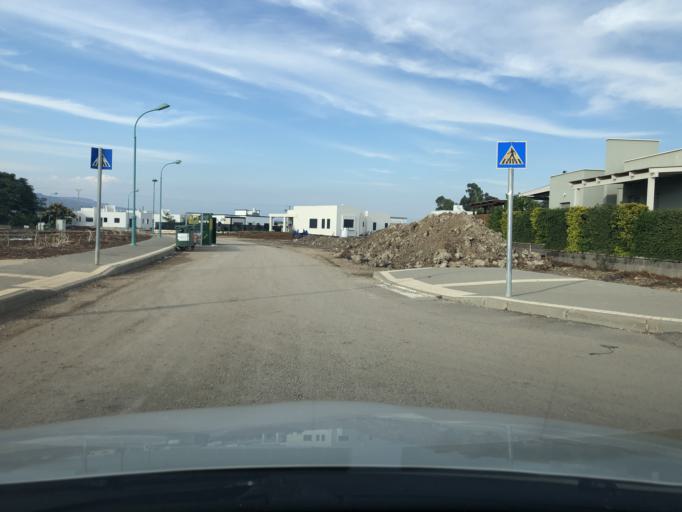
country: IL
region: Northern District
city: Yavne'el
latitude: 32.6619
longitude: 35.5865
